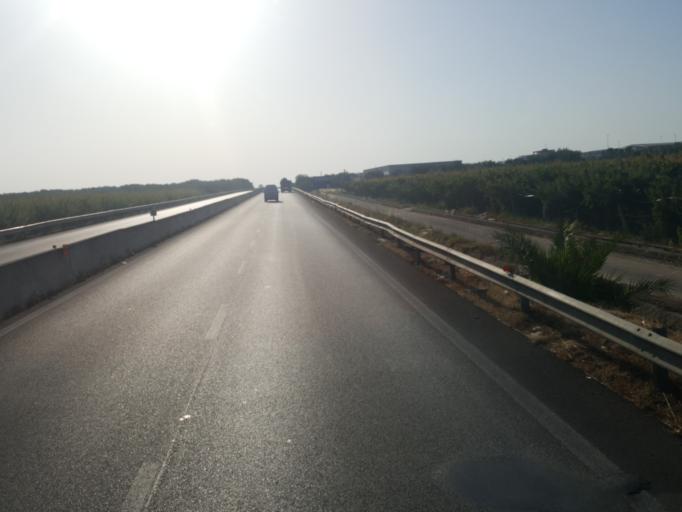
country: IT
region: Apulia
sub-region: Provincia di Barletta - Andria - Trani
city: San Ferdinando di Puglia
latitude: 41.3109
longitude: 16.0770
